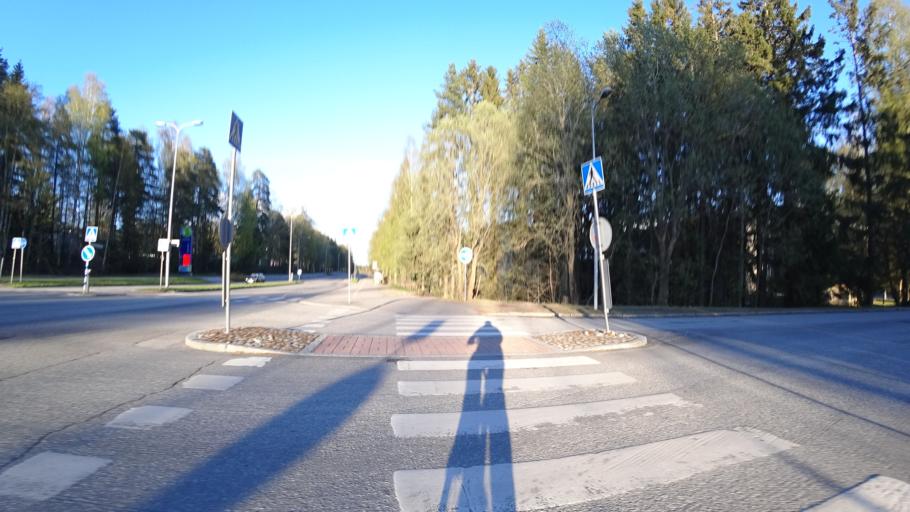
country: FI
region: Pirkanmaa
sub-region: Tampere
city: Pirkkala
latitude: 61.5044
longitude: 23.6180
